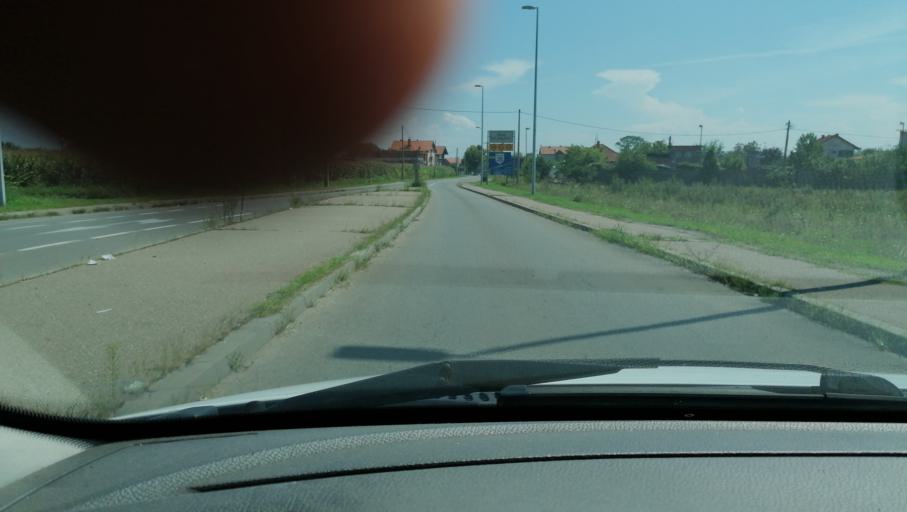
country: BA
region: Republika Srpska
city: Bijeljina
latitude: 44.7737
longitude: 19.2011
